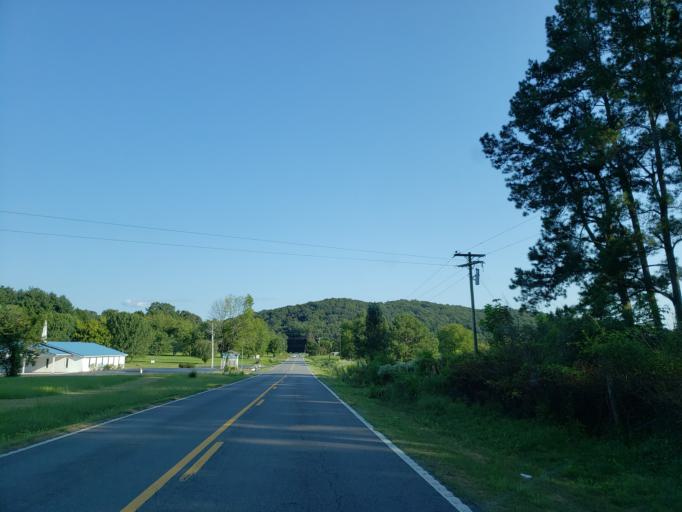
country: US
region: Tennessee
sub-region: Bradley County
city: Wildwood Lake
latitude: 35.0083
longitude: -84.7873
